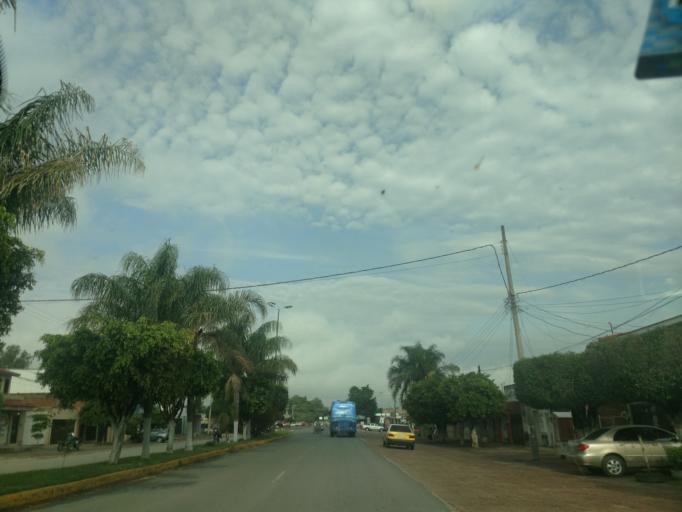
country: MX
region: Jalisco
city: Ameca
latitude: 20.5380
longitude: -104.0427
